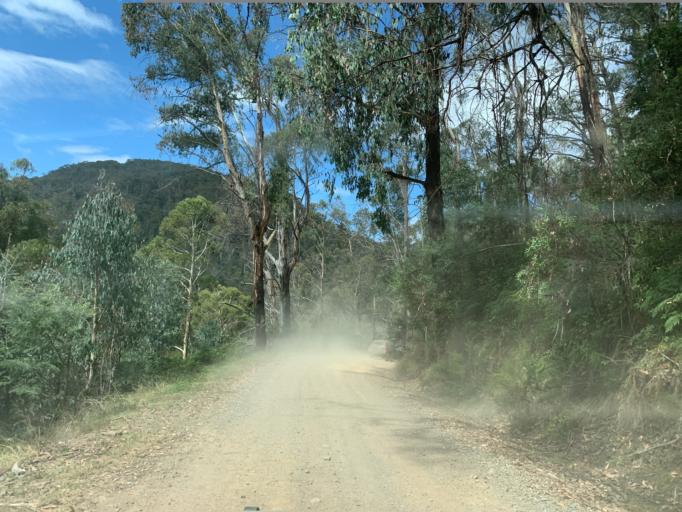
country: AU
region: Victoria
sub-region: Mansfield
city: Mansfield
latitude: -37.1007
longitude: 146.4989
